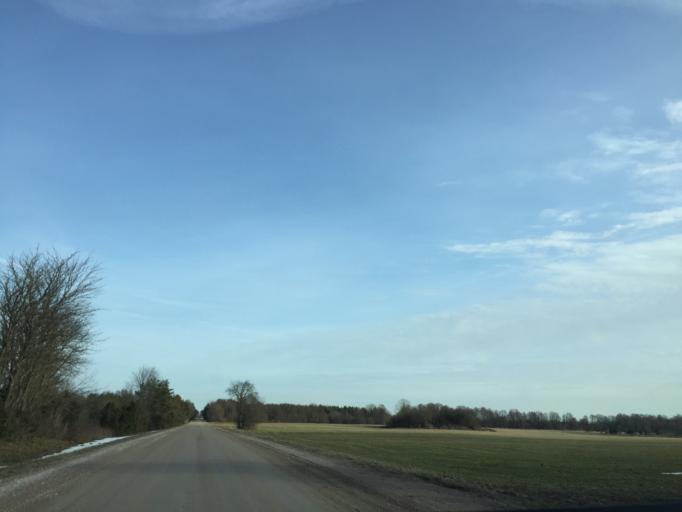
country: EE
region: Saare
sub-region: Kuressaare linn
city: Kuressaare
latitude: 58.3241
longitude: 22.0073
